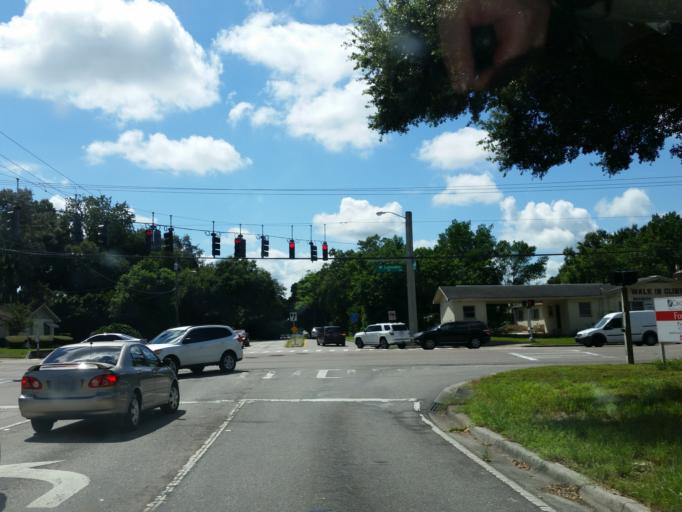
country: US
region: Florida
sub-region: Hillsborough County
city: Brandon
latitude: 27.9235
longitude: -82.2858
